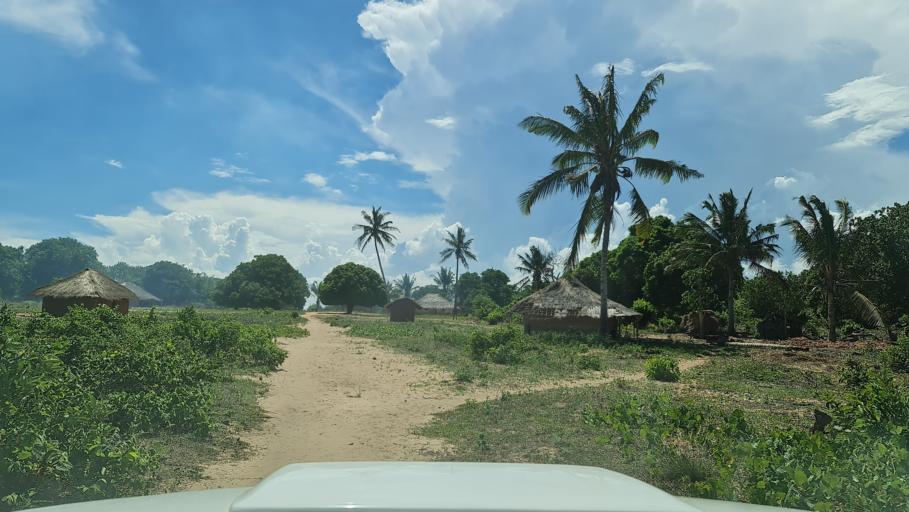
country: MZ
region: Nampula
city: Antonio Enes
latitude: -15.7057
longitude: 40.2617
